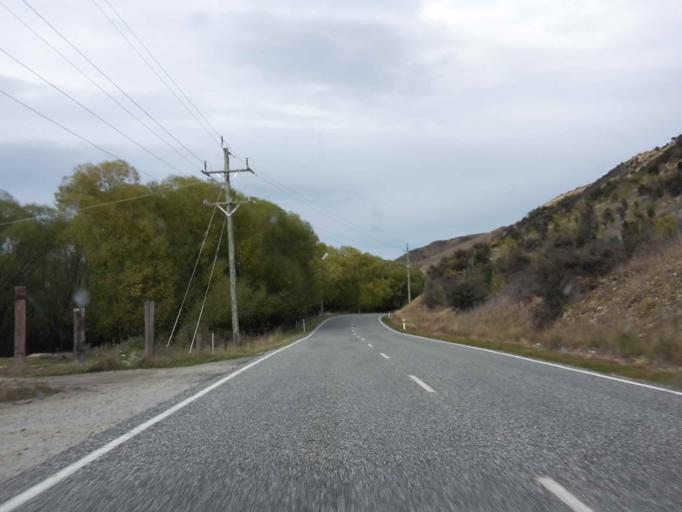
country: NZ
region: Otago
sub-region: Queenstown-Lakes District
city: Wanaka
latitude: -44.7861
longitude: 169.0829
